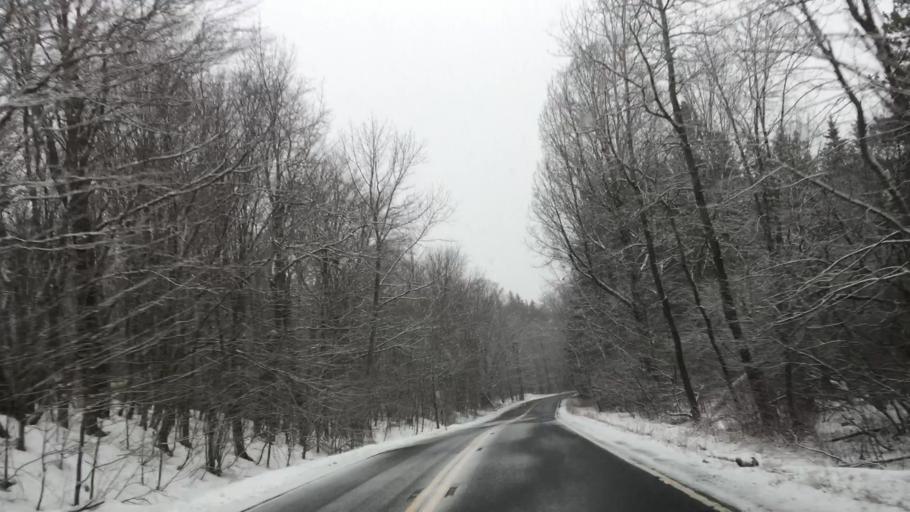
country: US
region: Massachusetts
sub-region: Berkshire County
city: Hinsdale
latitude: 42.4090
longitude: -73.1811
